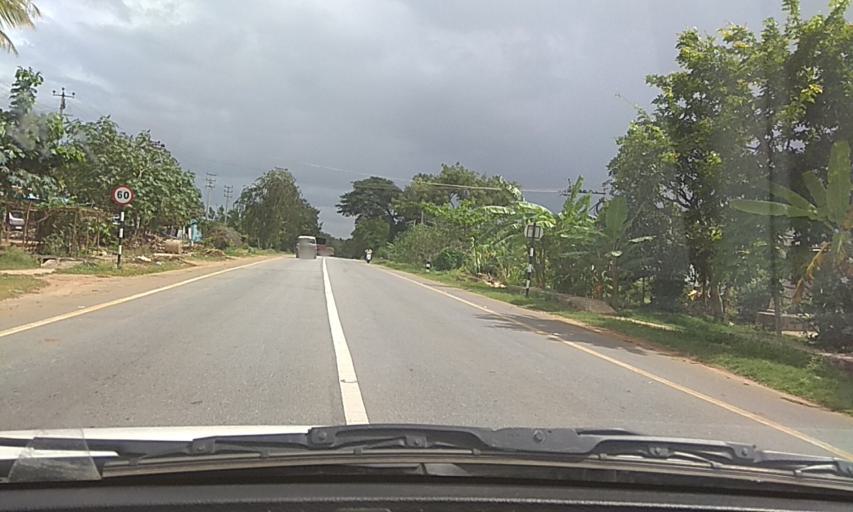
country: IN
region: Karnataka
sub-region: Tumkur
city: Kunigal
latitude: 13.0595
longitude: 77.0274
